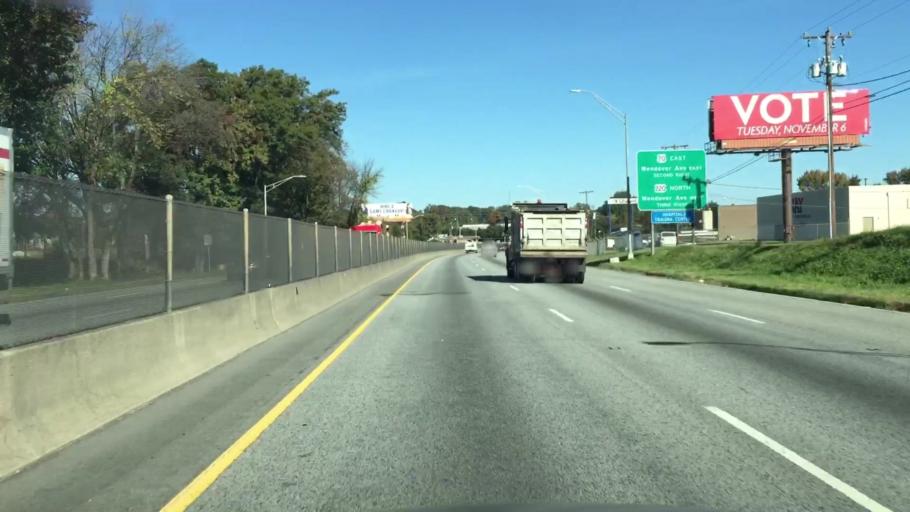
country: US
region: North Carolina
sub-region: Guilford County
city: Greensboro
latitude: 36.0811
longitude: -79.7673
